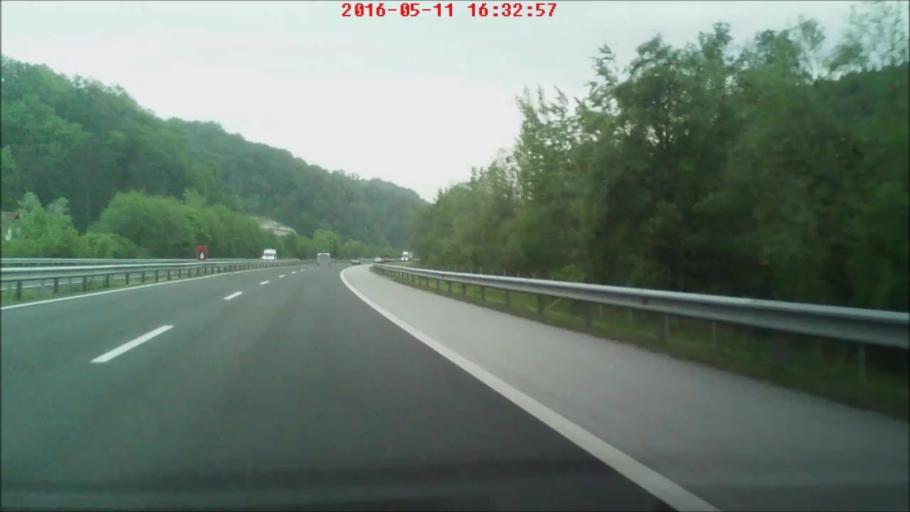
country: SI
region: Pesnica
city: Pesnica pri Mariboru
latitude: 46.6372
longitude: 15.6551
